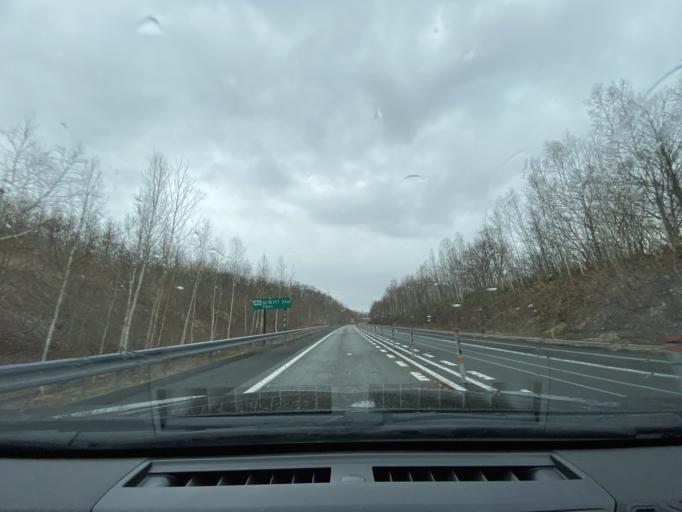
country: JP
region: Hokkaido
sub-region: Asahikawa-shi
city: Asahikawa
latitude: 43.9442
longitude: 142.4711
